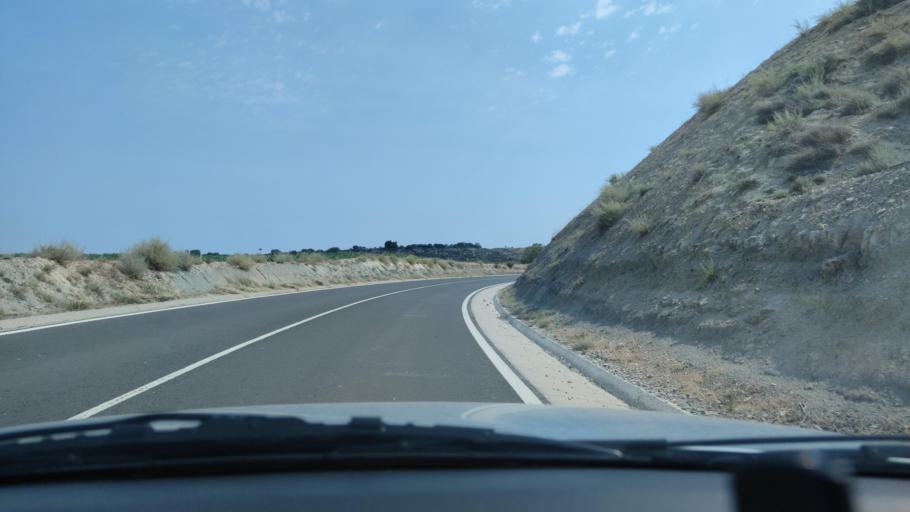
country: ES
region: Catalonia
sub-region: Provincia de Lleida
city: Nalec
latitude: 41.5918
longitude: 1.0848
